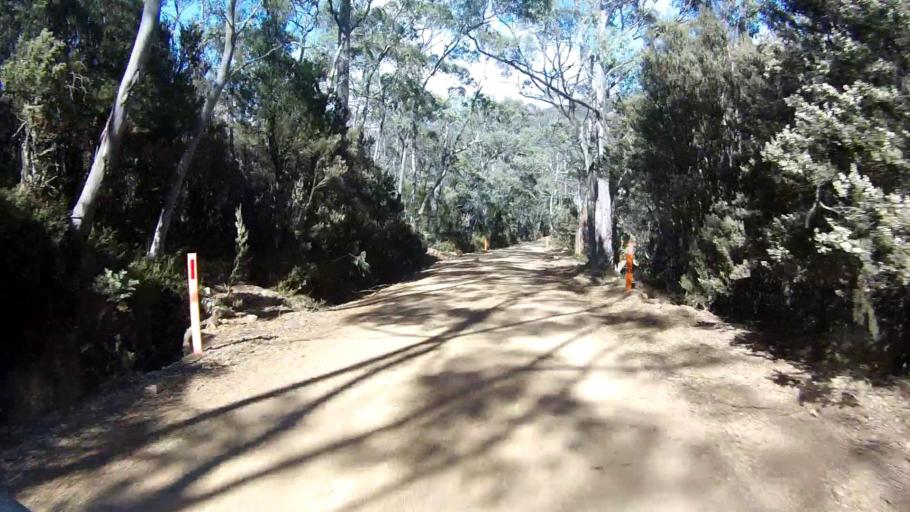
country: AU
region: Tasmania
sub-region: Derwent Valley
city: New Norfolk
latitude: -42.6854
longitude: 146.6053
